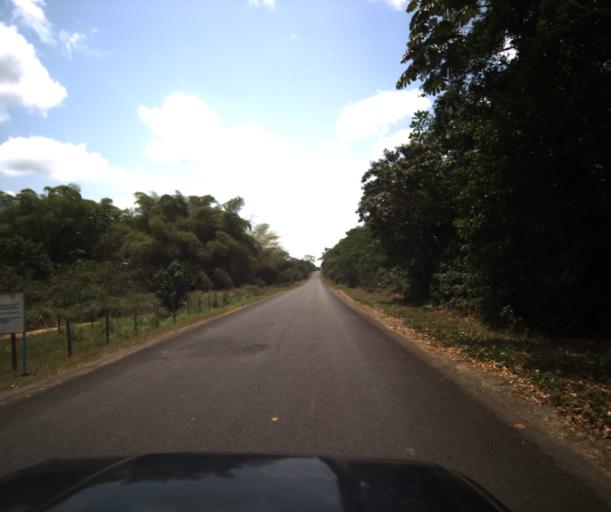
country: CM
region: Centre
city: Eseka
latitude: 3.7242
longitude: 10.8028
